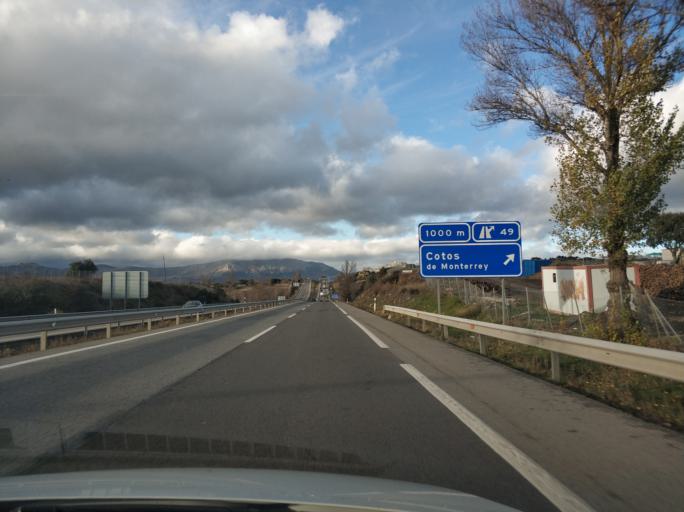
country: ES
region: Madrid
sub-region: Provincia de Madrid
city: Venturada
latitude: 40.7728
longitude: -3.6080
